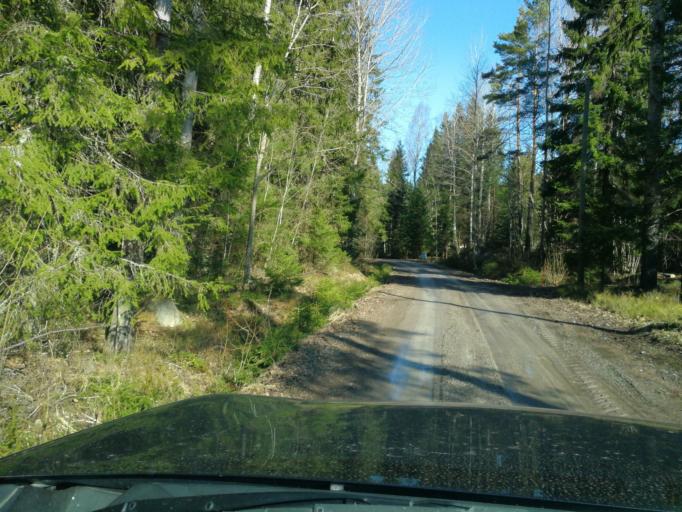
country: FI
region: Uusimaa
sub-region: Helsinki
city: Karjalohja
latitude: 60.2061
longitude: 23.7064
